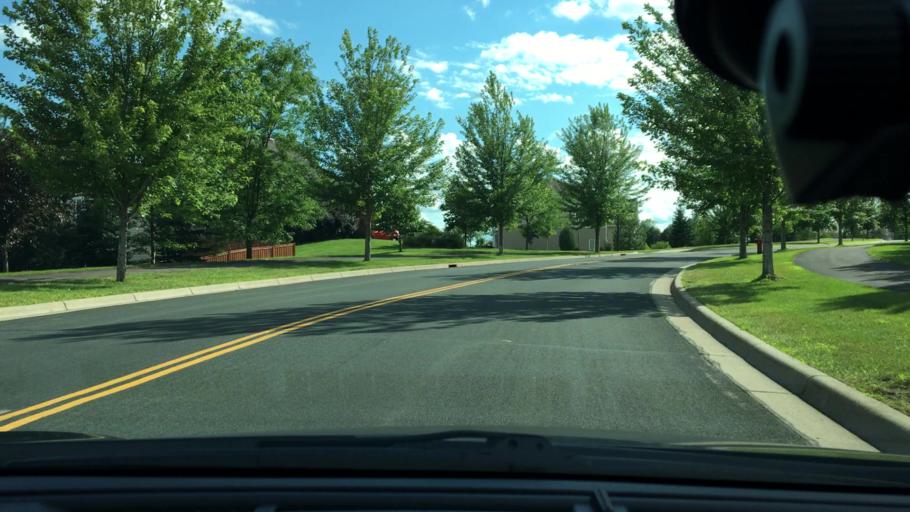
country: US
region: Minnesota
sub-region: Carver County
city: Victoria
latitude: 44.8591
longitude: -93.6799
